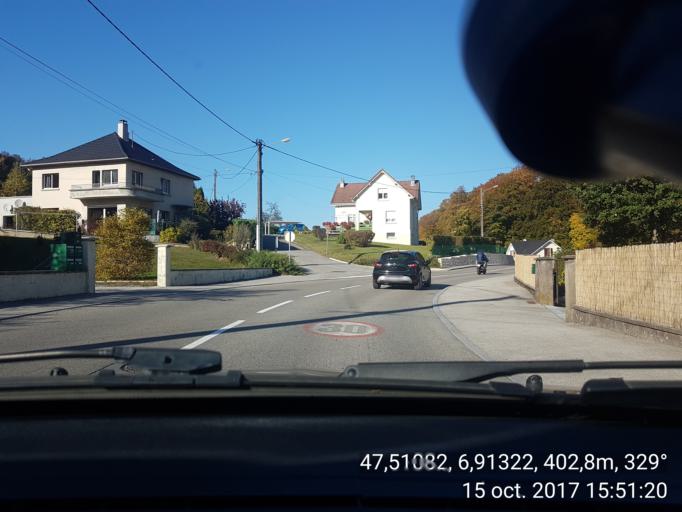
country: FR
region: Franche-Comte
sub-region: Departement du Doubs
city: Dampierre-les-Bois
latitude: 47.5107
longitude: 6.9132
